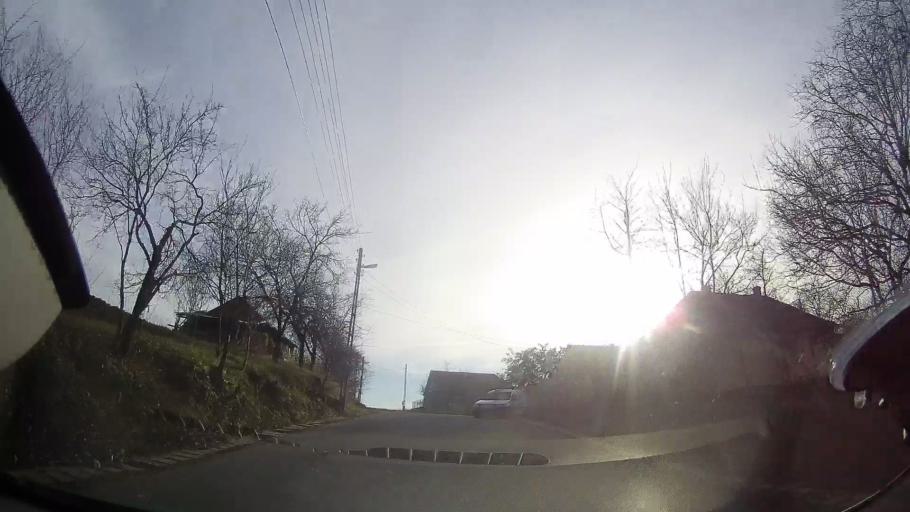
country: RO
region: Bihor
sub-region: Comuna Sarbi
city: Burzuc
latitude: 47.1383
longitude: 22.1836
